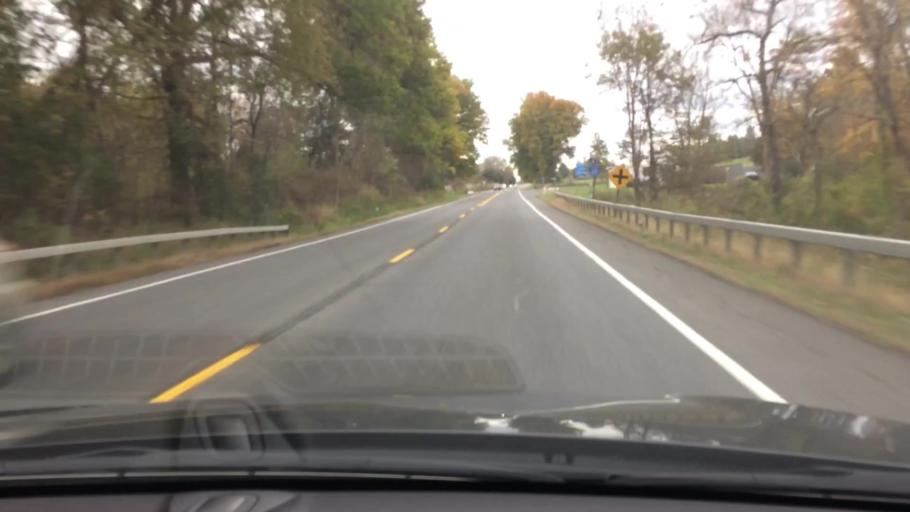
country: US
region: New York
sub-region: Columbia County
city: Stottville
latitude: 42.3204
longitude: -73.7024
